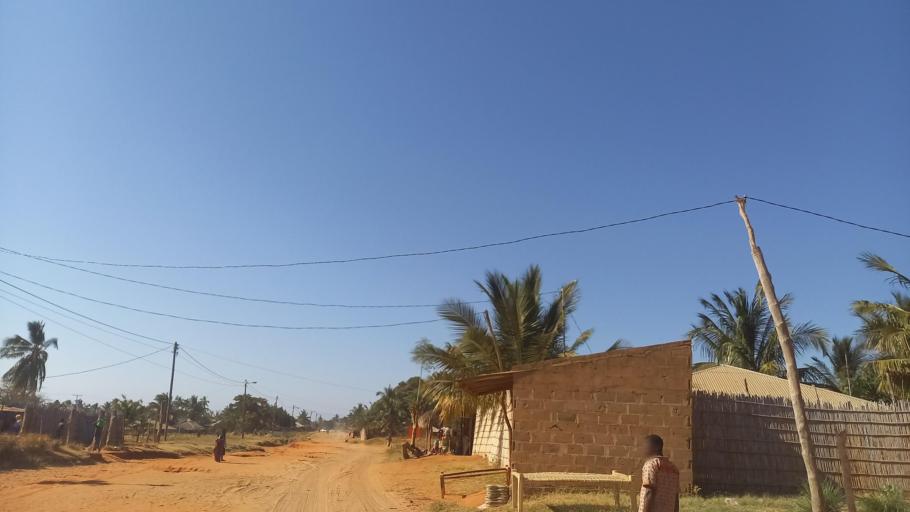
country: MZ
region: Cabo Delgado
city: Pemba
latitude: -13.1376
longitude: 40.5504
